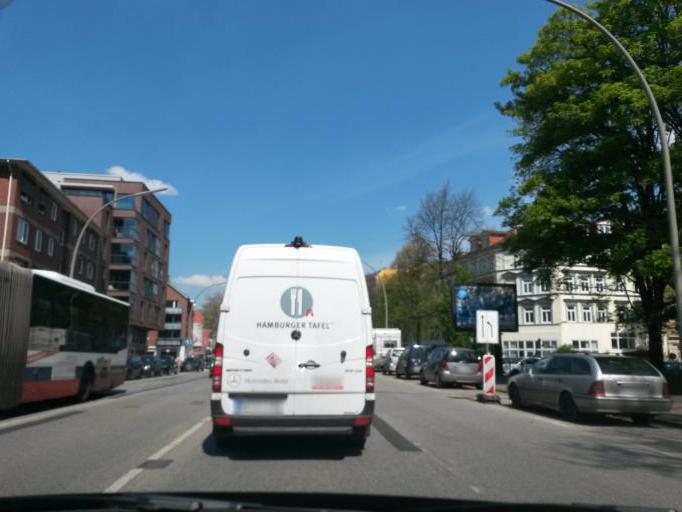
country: DE
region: Hamburg
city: St. Pauli
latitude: 53.5727
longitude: 9.9581
